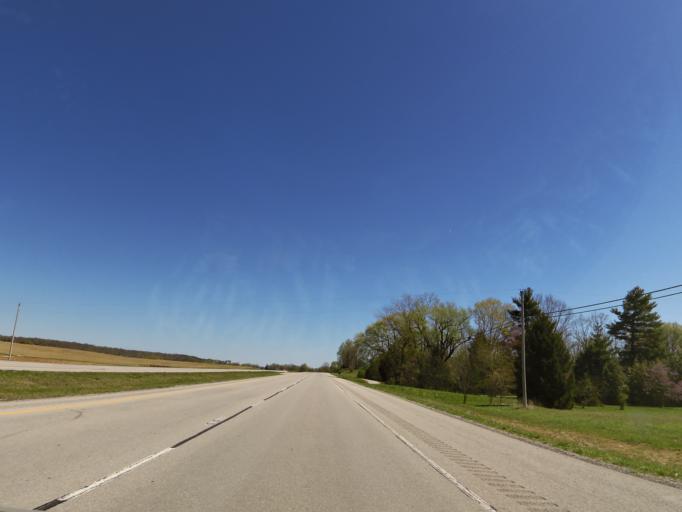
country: US
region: Kentucky
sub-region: Warren County
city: Bowling Green
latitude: 36.9173
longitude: -86.5636
